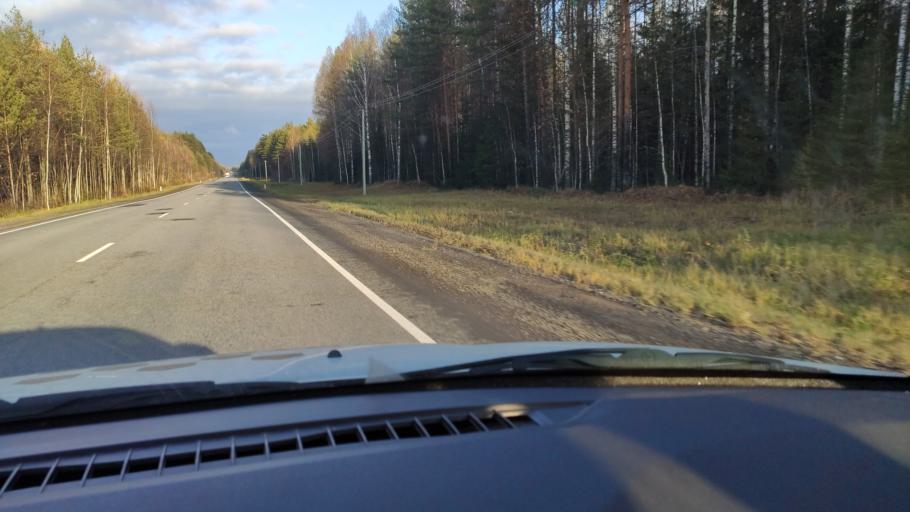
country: RU
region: Kirov
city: Belaya Kholunitsa
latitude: 58.9067
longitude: 51.0411
